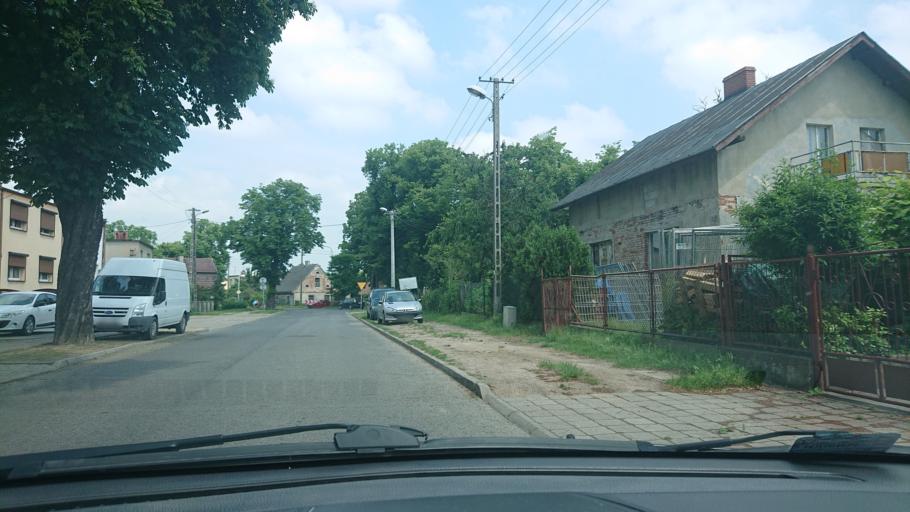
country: PL
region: Greater Poland Voivodeship
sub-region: Powiat gnieznienski
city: Gniezno
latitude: 52.5218
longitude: 17.5811
